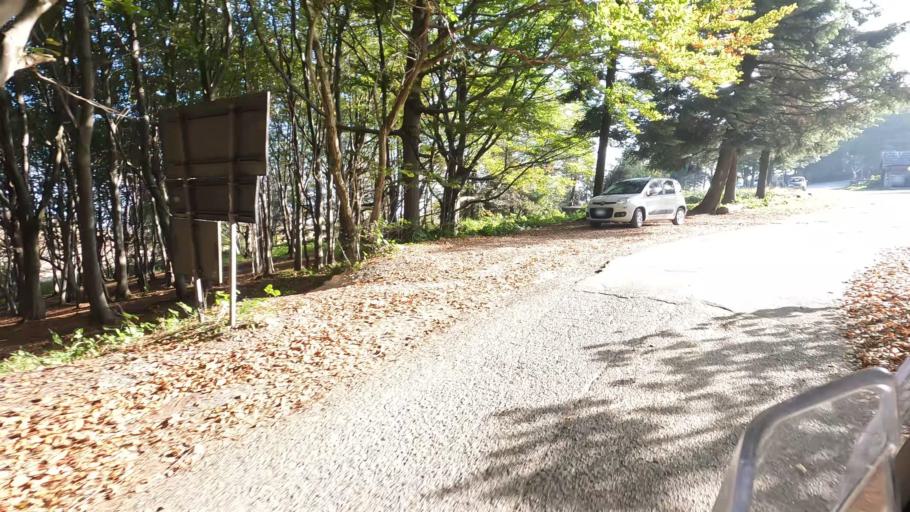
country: IT
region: Liguria
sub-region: Provincia di Genova
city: Sciarborasca
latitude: 44.4289
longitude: 8.5874
